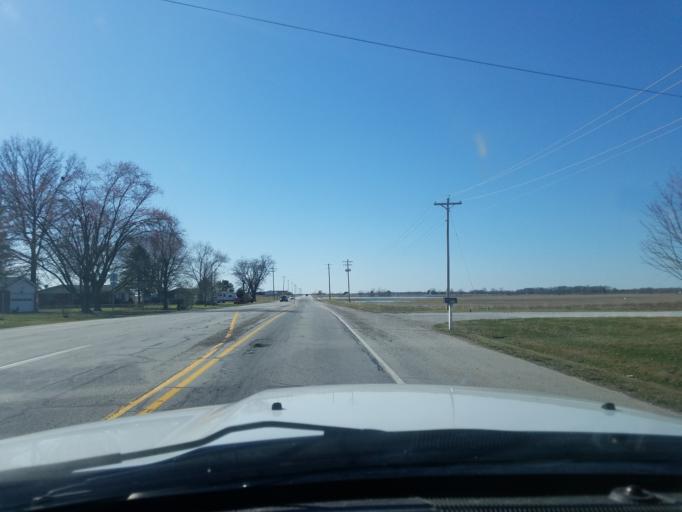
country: US
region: Indiana
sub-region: Shelby County
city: Shelbyville
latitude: 39.5046
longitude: -85.8037
